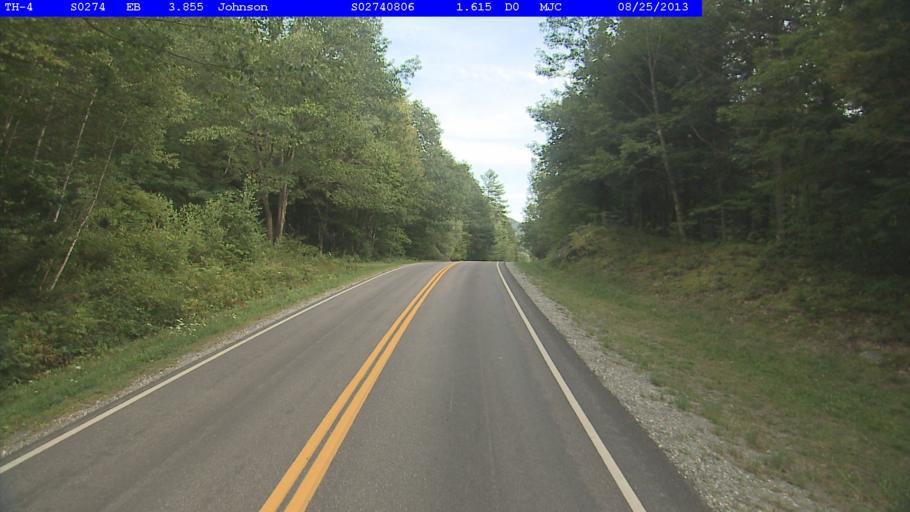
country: US
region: Vermont
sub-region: Lamoille County
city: Johnson
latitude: 44.6480
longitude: -72.7229
